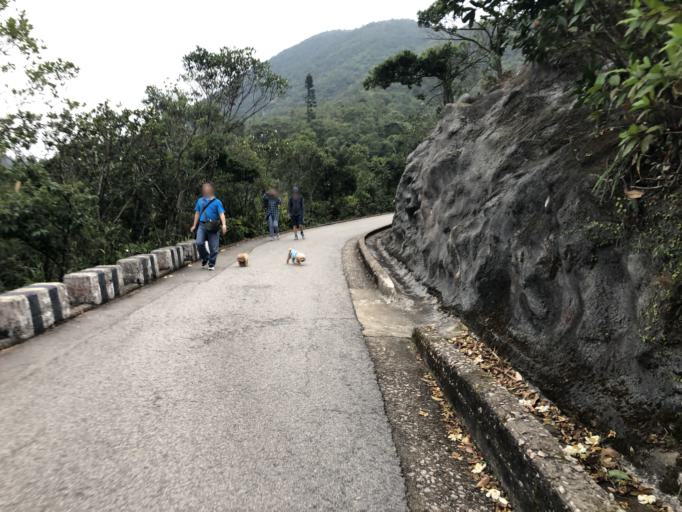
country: HK
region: Wanchai
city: Wan Chai
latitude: 22.2720
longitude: 114.2104
